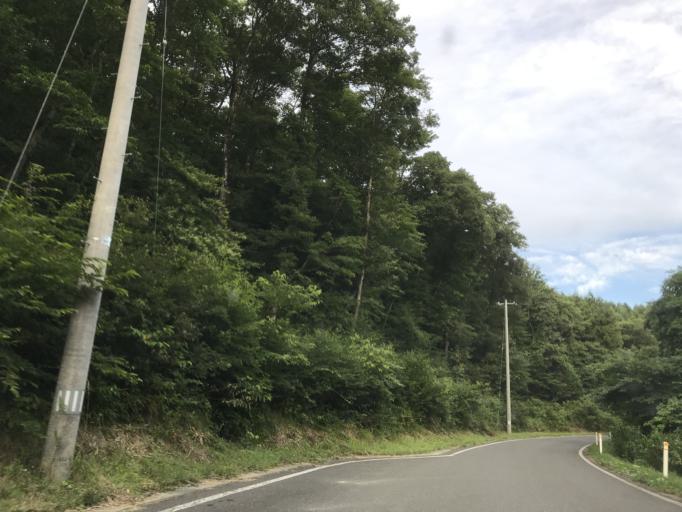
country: JP
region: Iwate
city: Ichinoseki
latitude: 38.9137
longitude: 141.0340
